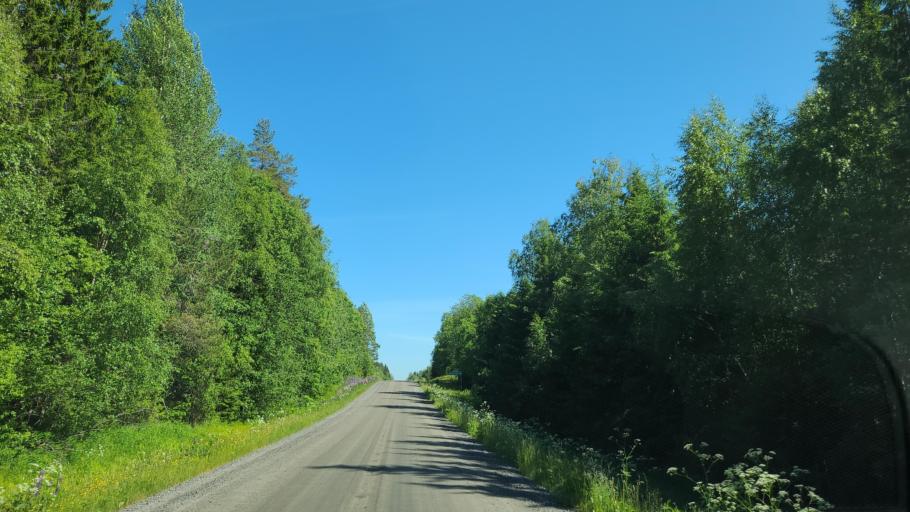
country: SE
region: Vaesterbotten
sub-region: Bjurholms Kommun
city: Bjurholm
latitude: 63.6420
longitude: 19.1292
